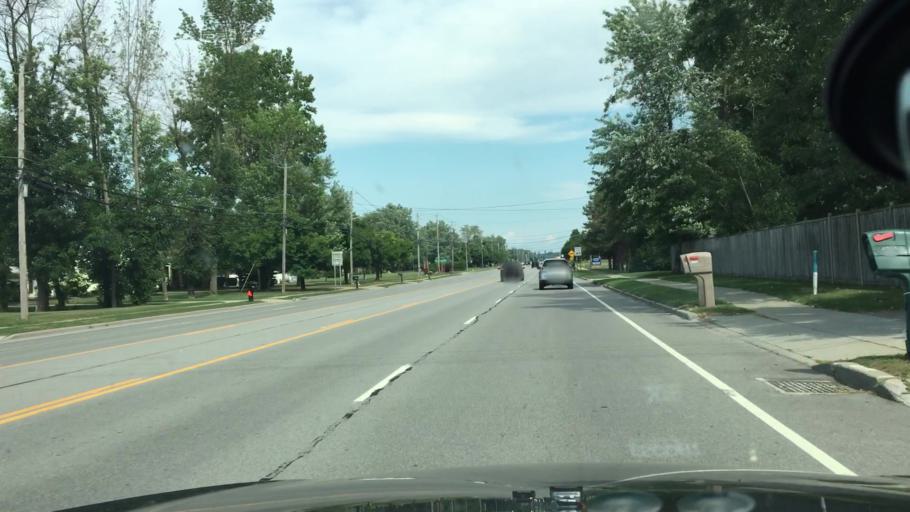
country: US
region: New York
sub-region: Erie County
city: Williamsville
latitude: 42.9786
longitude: -78.7500
